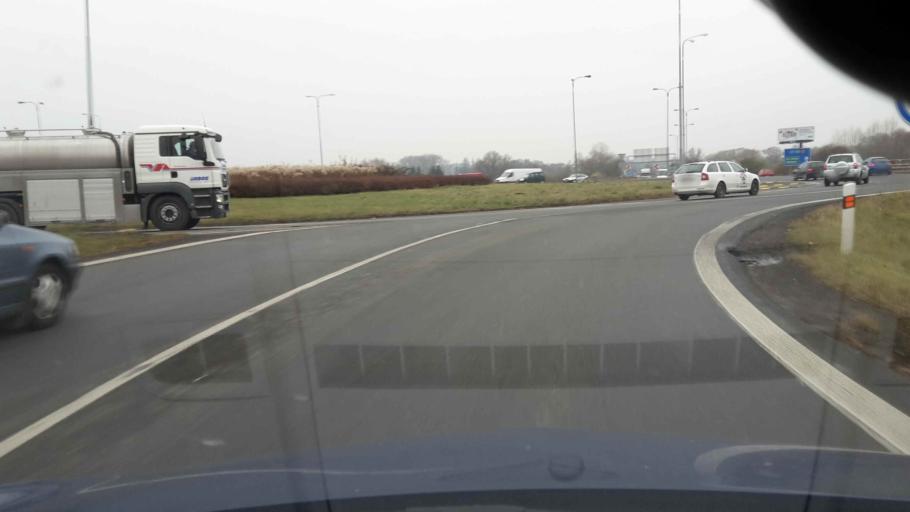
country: CZ
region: Olomoucky
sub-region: Okres Olomouc
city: Olomouc
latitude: 49.6041
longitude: 17.2200
